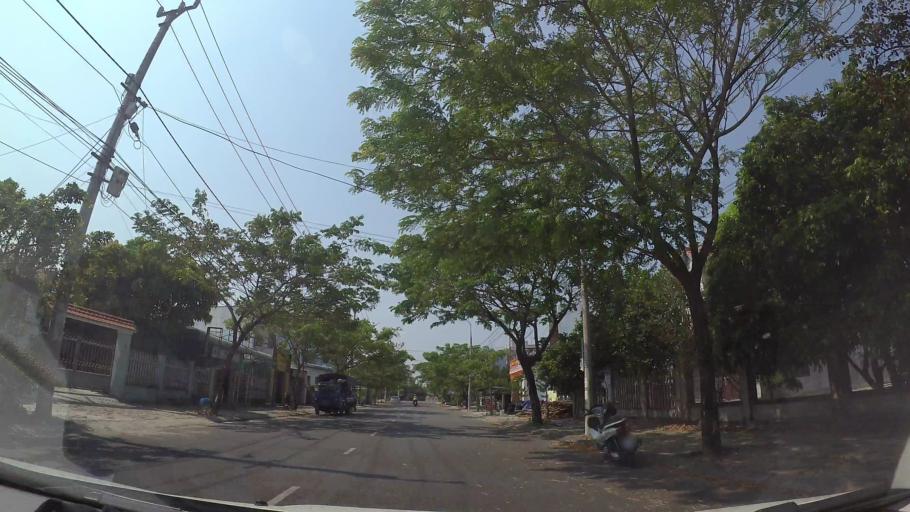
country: VN
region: Da Nang
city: Ngu Hanh Son
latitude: 15.9831
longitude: 108.2724
